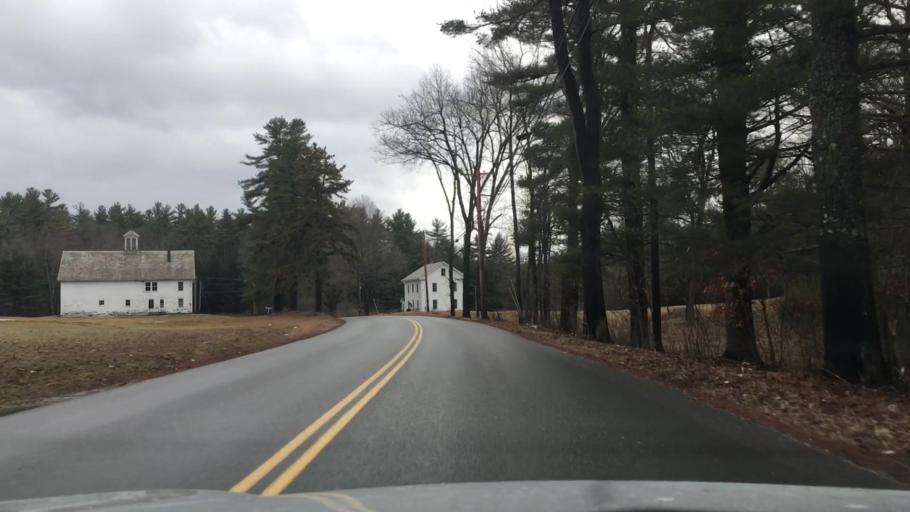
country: US
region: Massachusetts
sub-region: Worcester County
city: Athol
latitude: 42.5769
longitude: -72.2529
